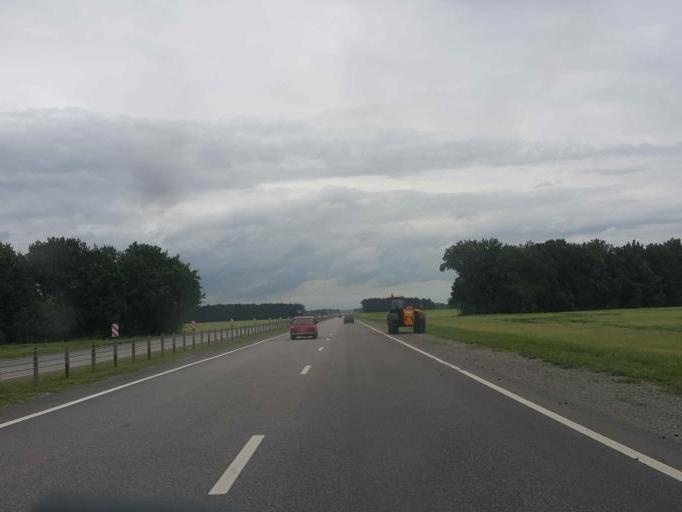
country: RU
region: Tambov
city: Zavoronezhskoye
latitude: 52.8963
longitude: 40.6775
